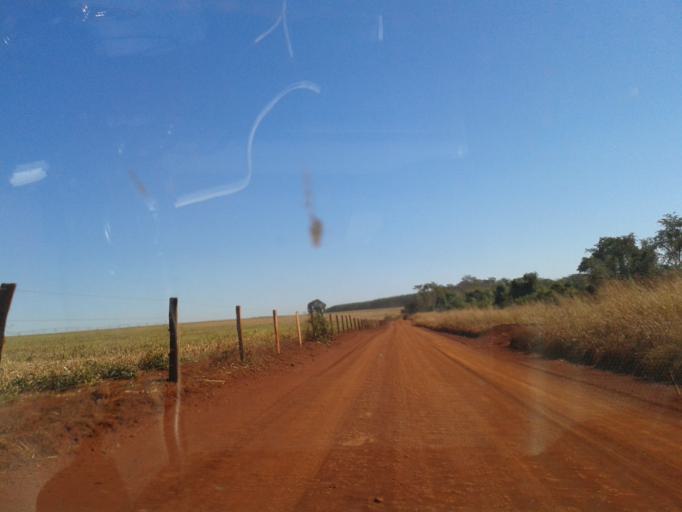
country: BR
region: Minas Gerais
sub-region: Centralina
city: Centralina
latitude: -18.5810
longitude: -49.1313
